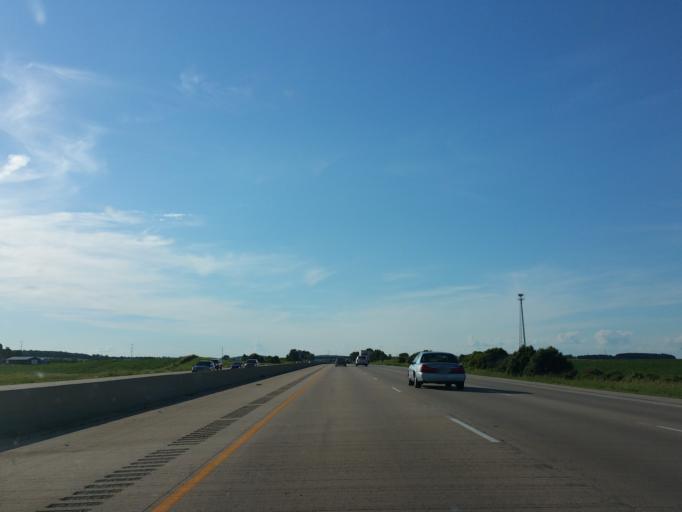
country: US
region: Wisconsin
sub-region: Dane County
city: De Forest
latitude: 43.2701
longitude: -89.3937
